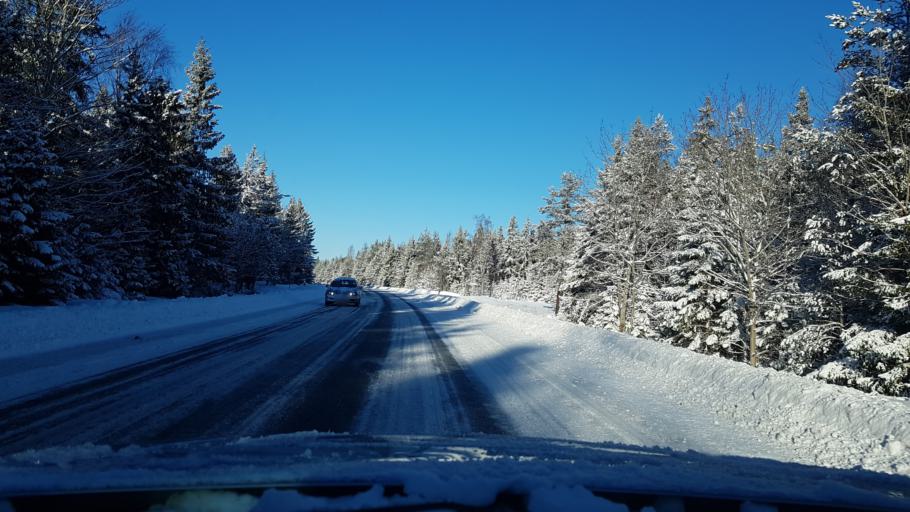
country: EE
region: Hiiumaa
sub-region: Kaerdla linn
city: Kardla
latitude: 58.9810
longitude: 22.8088
